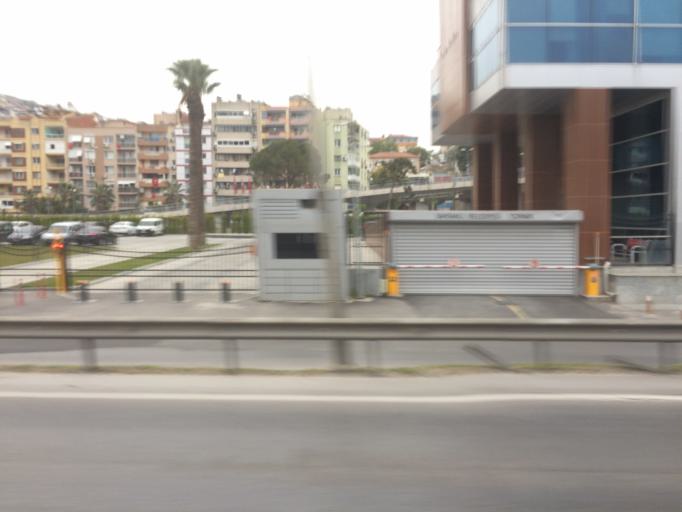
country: TR
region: Izmir
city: Karsiyaka
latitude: 38.4647
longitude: 27.1623
